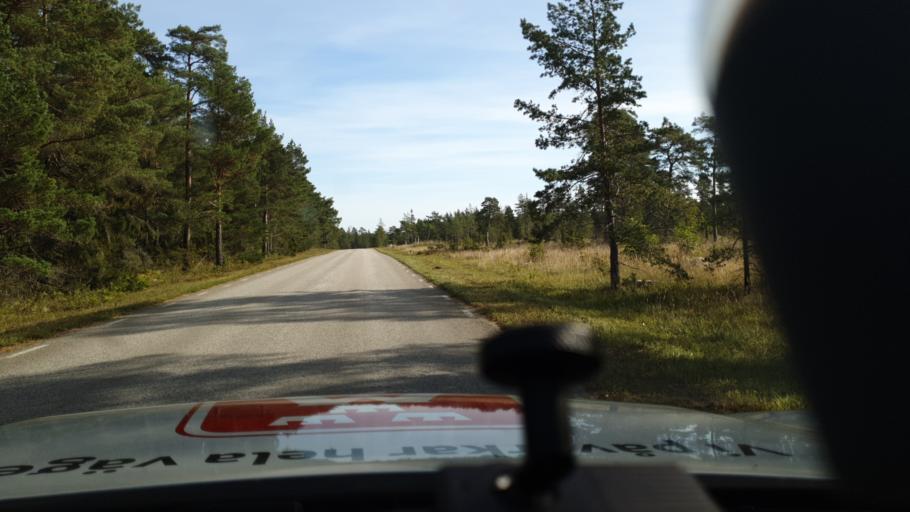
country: SE
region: Gotland
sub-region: Gotland
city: Slite
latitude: 57.8563
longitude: 18.7078
